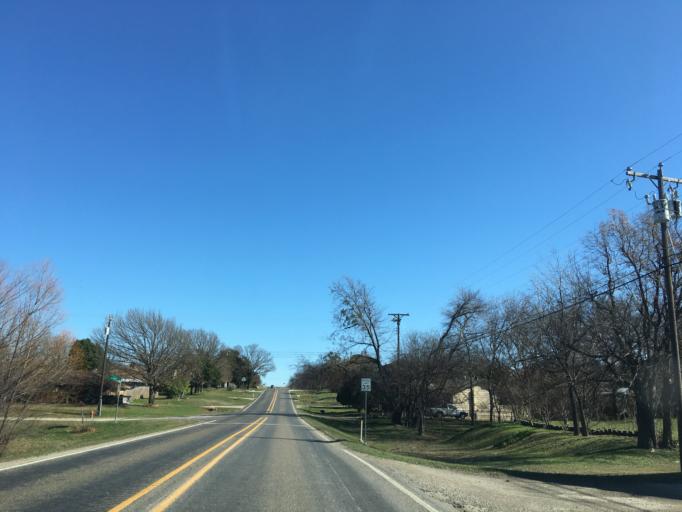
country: US
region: Texas
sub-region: Collin County
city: Prosper
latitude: 33.2359
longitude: -96.7995
